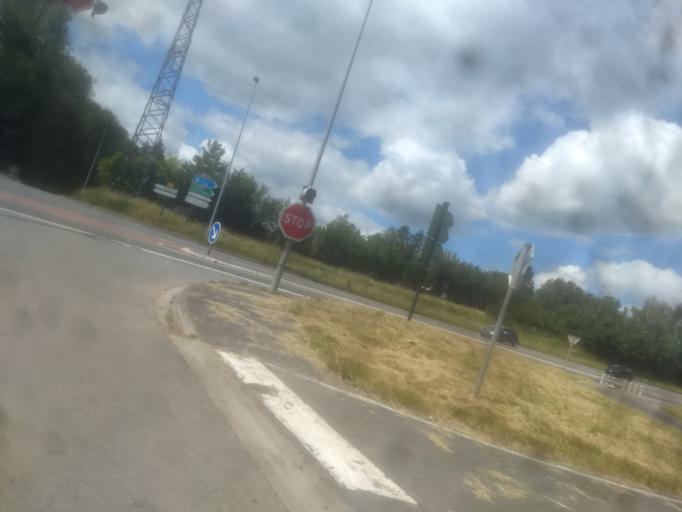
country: FR
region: Nord-Pas-de-Calais
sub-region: Departement du Pas-de-Calais
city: Maroeuil
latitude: 50.3120
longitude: 2.7211
